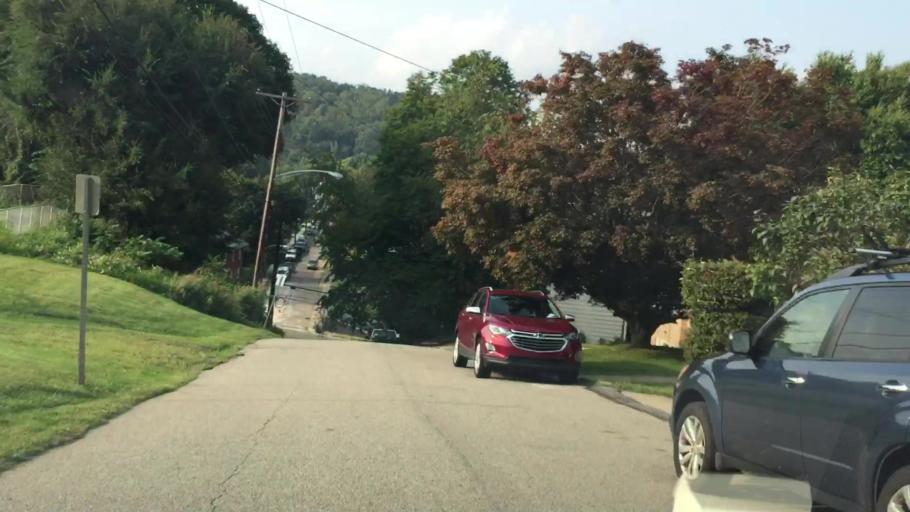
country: US
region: Pennsylvania
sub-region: Allegheny County
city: Emsworth
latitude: 40.5096
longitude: -80.0979
